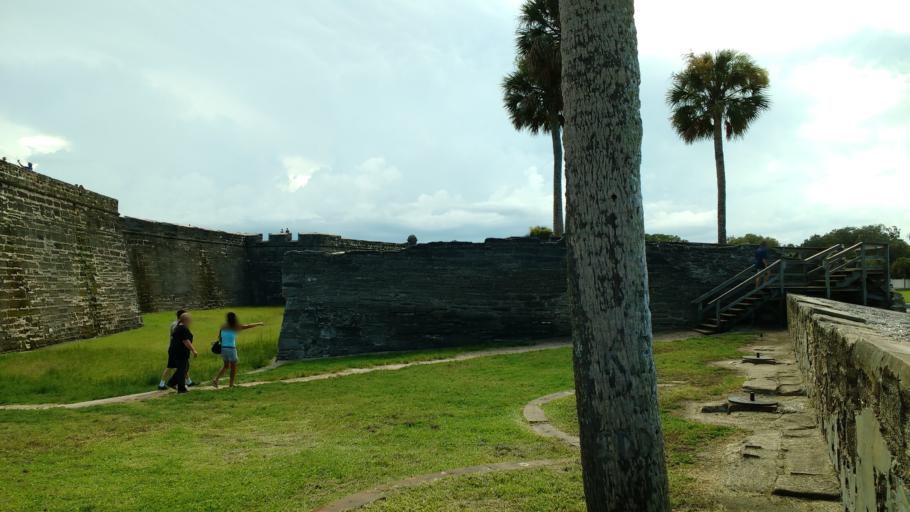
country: US
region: Florida
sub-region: Saint Johns County
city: Saint Augustine
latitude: 29.8985
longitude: -81.3108
